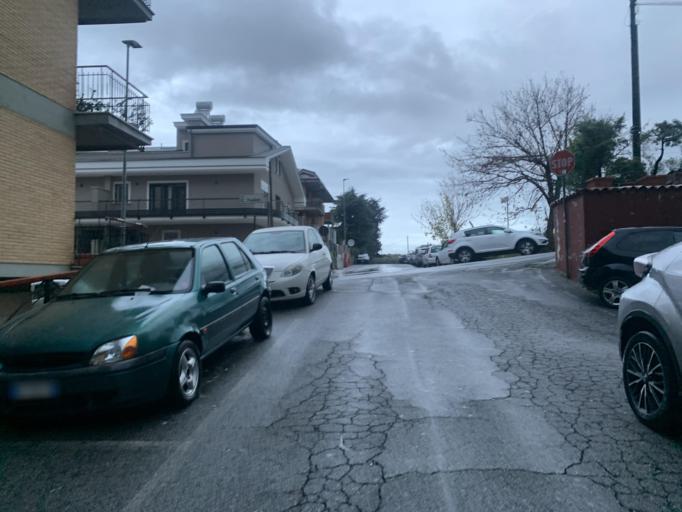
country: IT
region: Latium
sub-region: Citta metropolitana di Roma Capitale
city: Setteville
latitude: 41.9439
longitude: 12.6542
